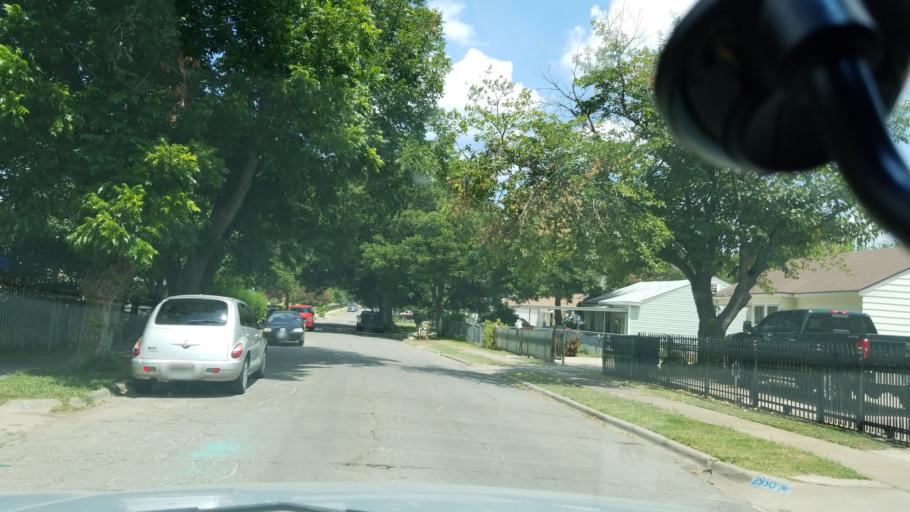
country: US
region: Texas
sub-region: Dallas County
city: Cockrell Hill
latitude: 32.7317
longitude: -96.8703
